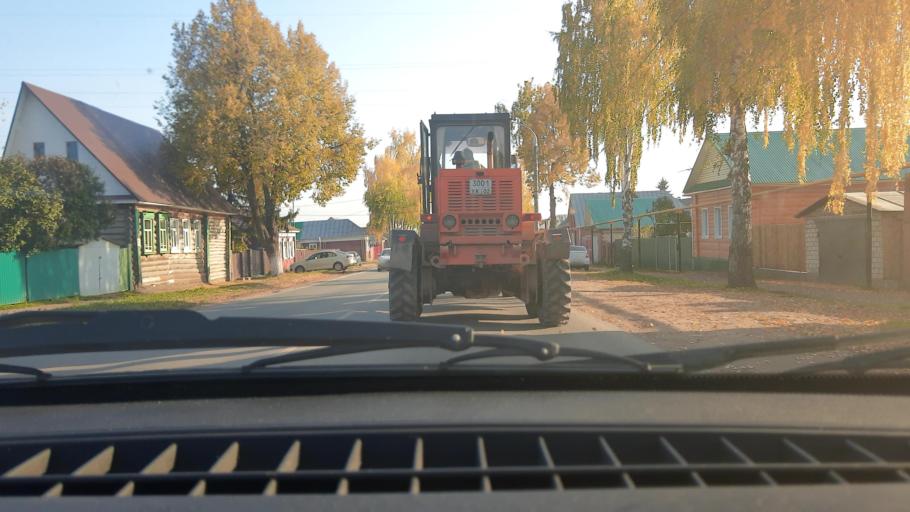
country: RU
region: Bashkortostan
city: Blagoveshchensk
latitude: 55.0388
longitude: 55.9629
